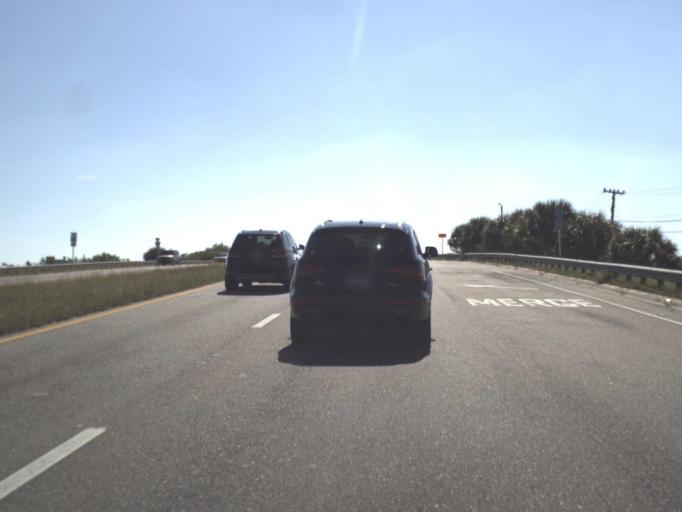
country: US
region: Florida
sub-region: Brevard County
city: Rockledge
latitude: 28.2942
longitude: -80.7430
